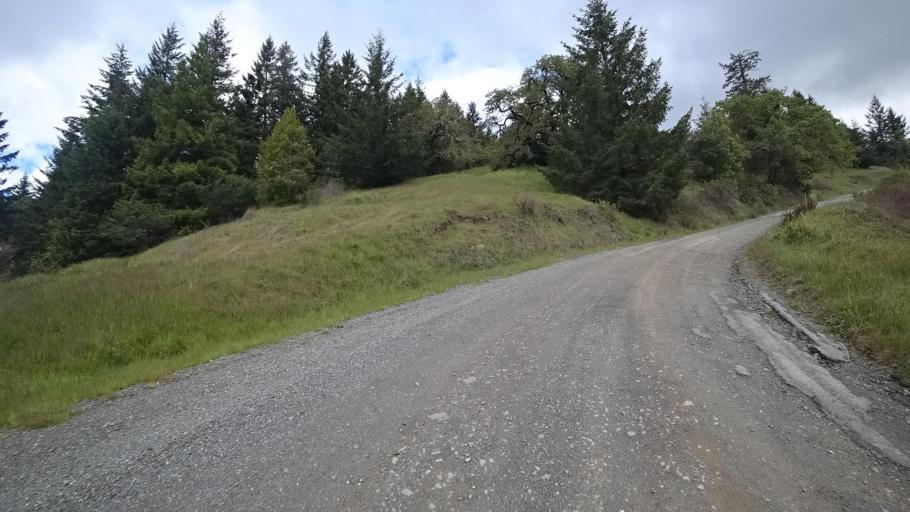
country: US
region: California
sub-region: Humboldt County
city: Blue Lake
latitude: 40.8559
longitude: -123.9172
